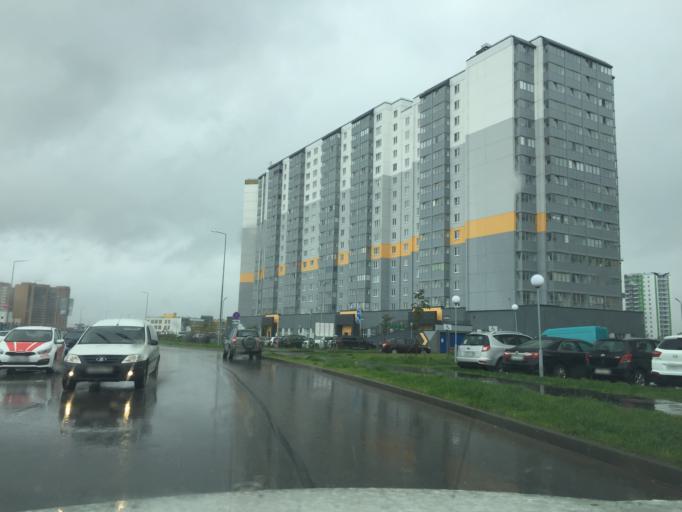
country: RU
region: St.-Petersburg
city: Gorelovo
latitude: 59.7888
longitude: 30.1629
